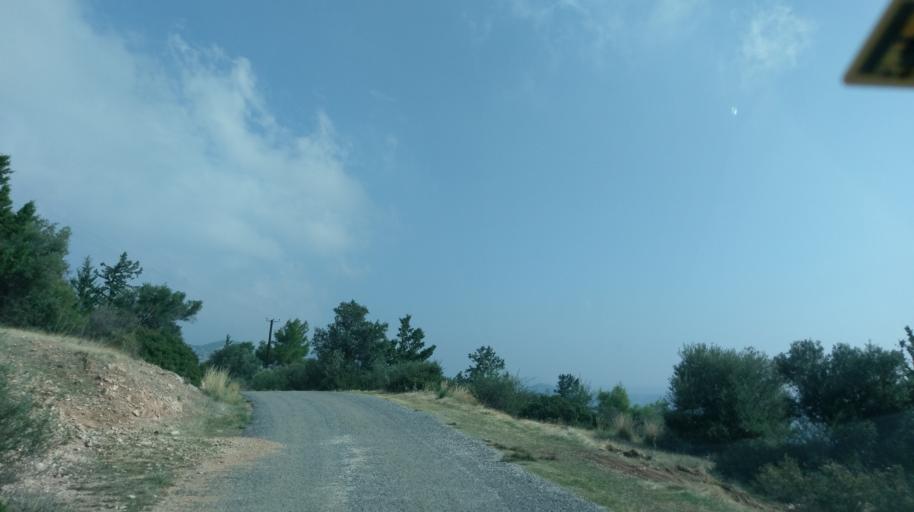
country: CY
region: Ammochostos
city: Lefkonoiko
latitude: 35.3169
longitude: 33.6211
